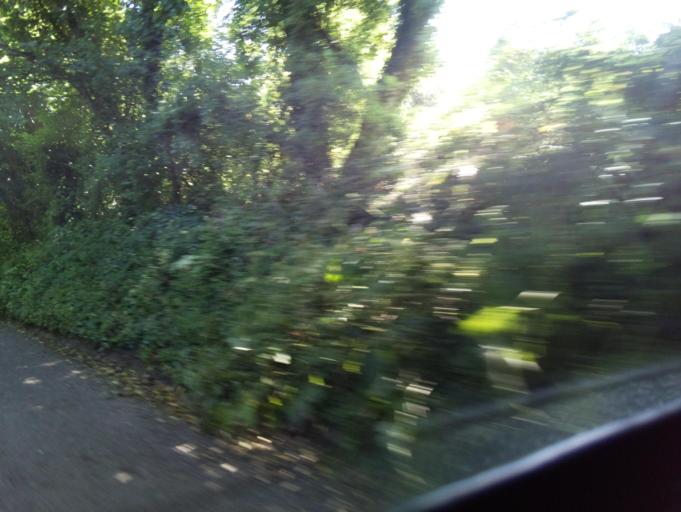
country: GB
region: England
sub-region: Borough of Torbay
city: Paignton
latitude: 50.4157
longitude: -3.5981
